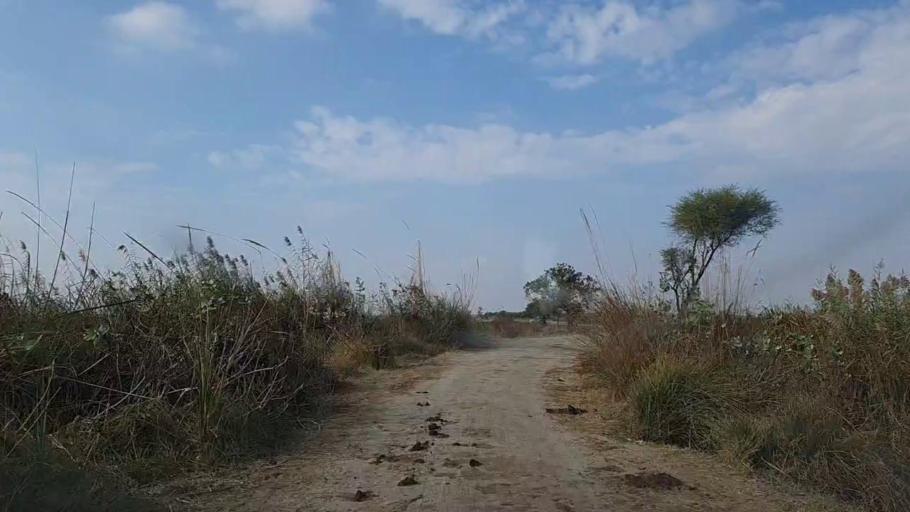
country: PK
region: Sindh
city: Sanghar
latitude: 26.2514
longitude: 69.0126
